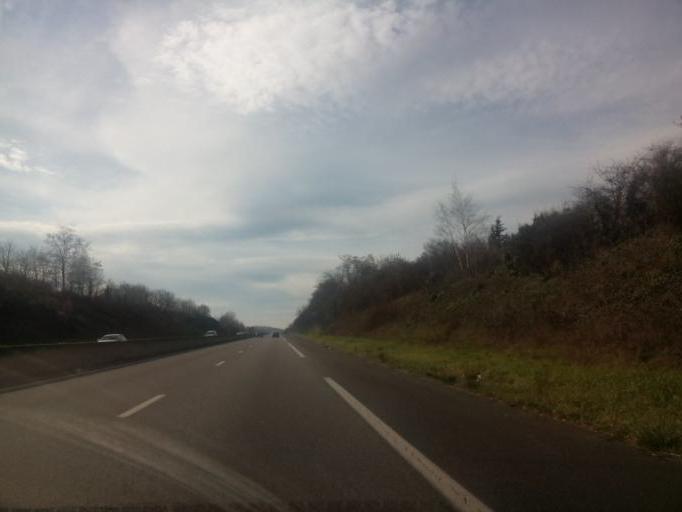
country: FR
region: Rhone-Alpes
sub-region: Departement du Rhone
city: Irigny
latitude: 45.6849
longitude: 4.8062
